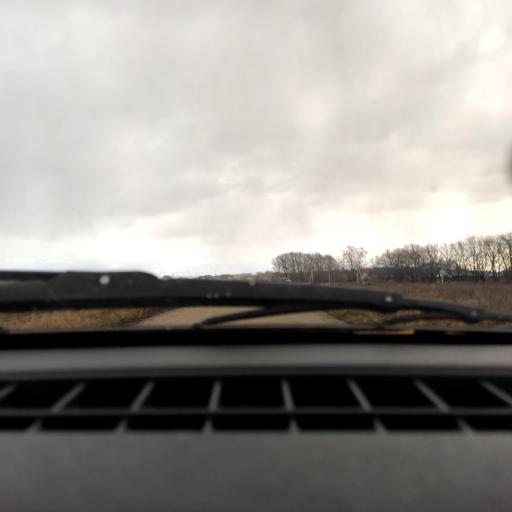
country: RU
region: Bashkortostan
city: Iglino
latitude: 54.7418
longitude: 56.3206
